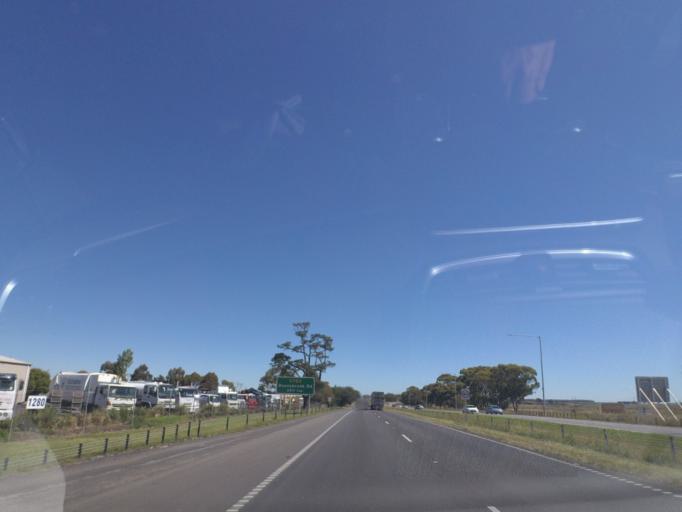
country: AU
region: Victoria
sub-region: Hume
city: Craigieburn
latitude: -37.5308
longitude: 144.9472
